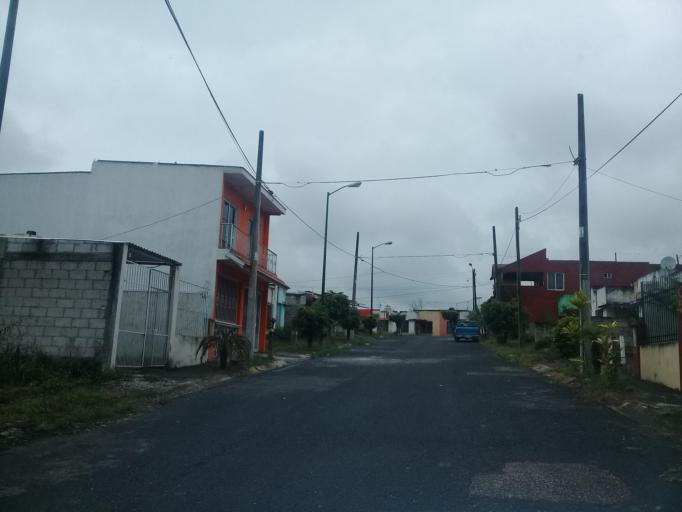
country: MX
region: Veracruz
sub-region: Cordoba
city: San Jose de Tapia
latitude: 18.8398
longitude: -96.9552
